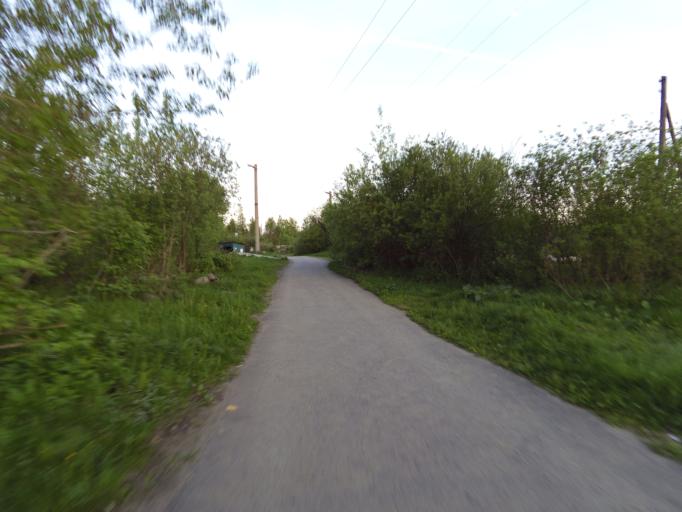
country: RU
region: Sverdlovsk
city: Shirokaya Rechka
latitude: 56.8446
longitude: 60.4988
